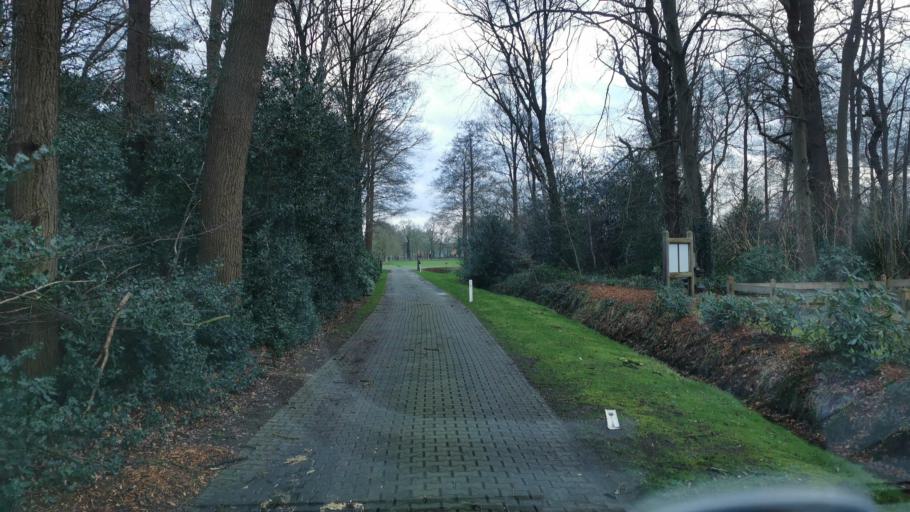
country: DE
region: Lower Saxony
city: Lage
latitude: 52.4426
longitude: 6.9803
